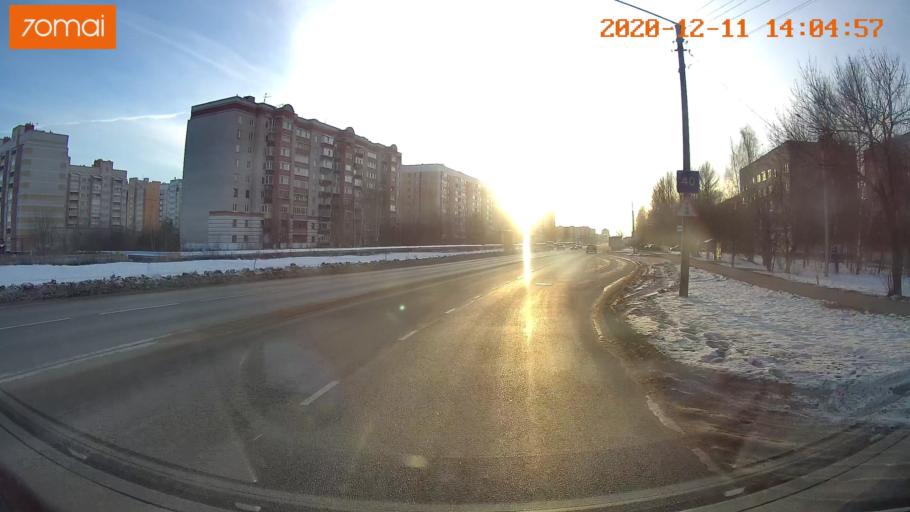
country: RU
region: Kostroma
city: Oktyabr'skiy
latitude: 57.7505
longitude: 41.0162
